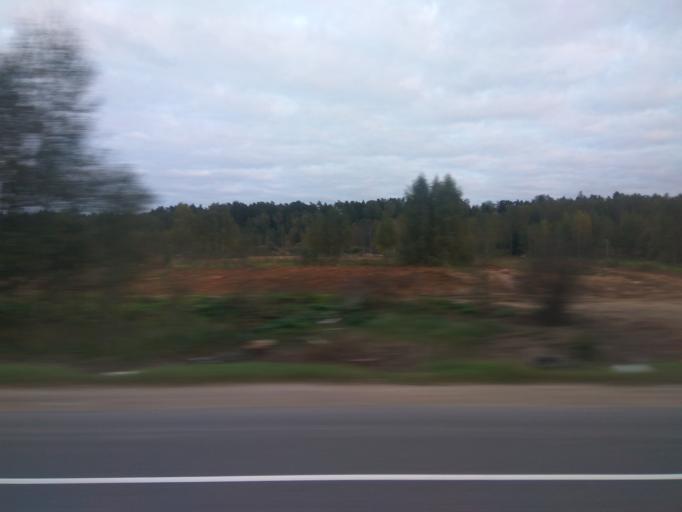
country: RU
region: Moskovskaya
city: Krasnoarmeysk
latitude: 56.0229
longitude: 38.1762
